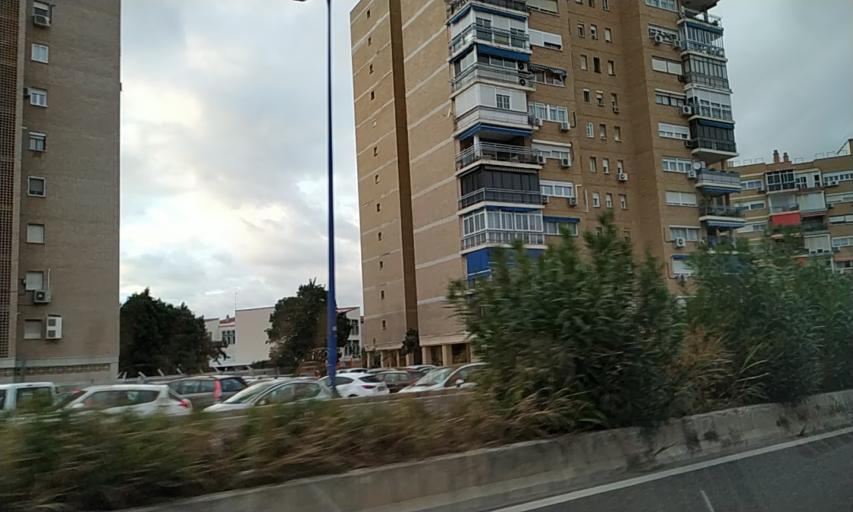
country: ES
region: Extremadura
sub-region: Provincia de Badajoz
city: Badajoz
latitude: 38.8757
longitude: -6.9814
